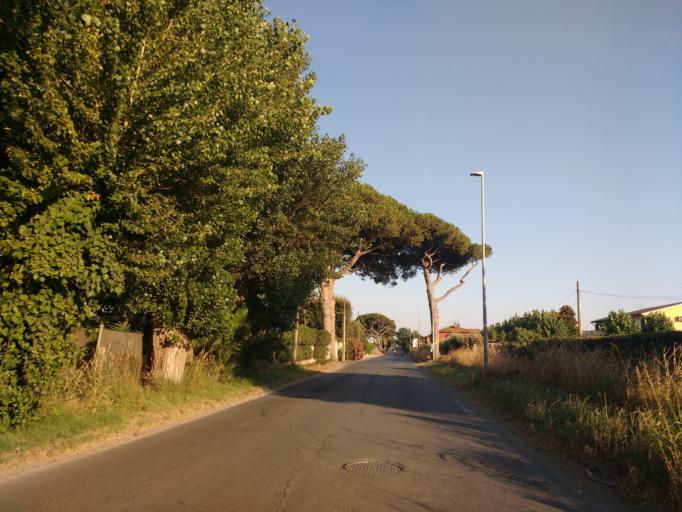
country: IT
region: Latium
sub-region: Citta metropolitana di Roma Capitale
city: Fregene
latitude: 41.8425
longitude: 12.2246
